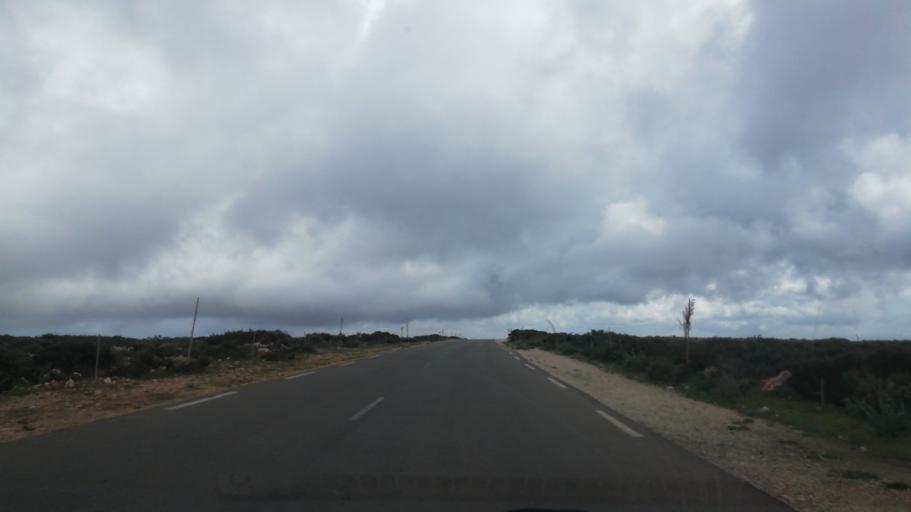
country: DZ
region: Oran
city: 'Ain el Turk
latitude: 35.6996
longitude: -0.7635
